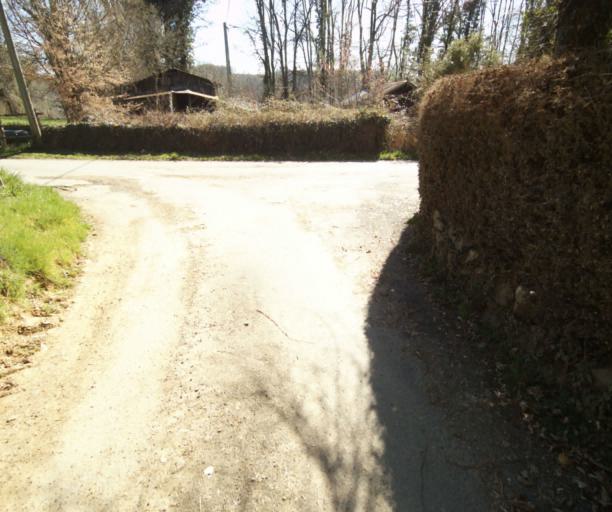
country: FR
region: Limousin
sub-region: Departement de la Correze
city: Chamboulive
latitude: 45.4259
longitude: 1.6376
